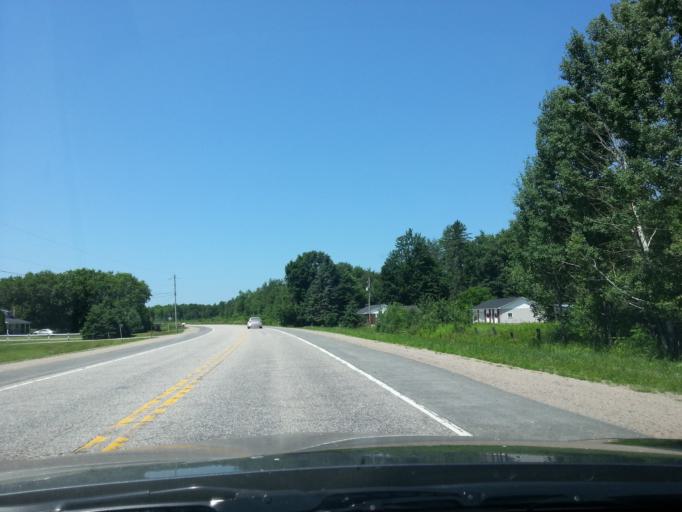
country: CA
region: Ontario
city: Arnprior
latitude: 45.5560
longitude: -76.1499
